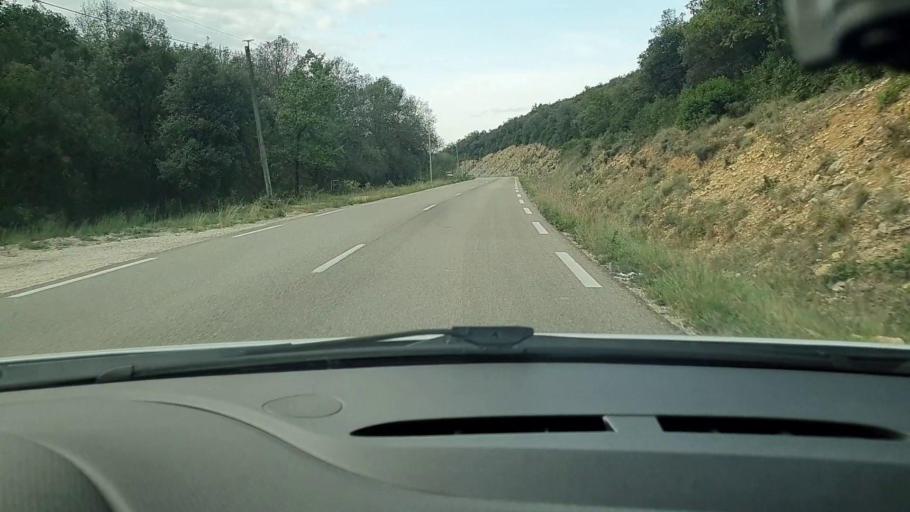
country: FR
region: Languedoc-Roussillon
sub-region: Departement du Gard
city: Mons
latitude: 44.0989
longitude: 4.2234
